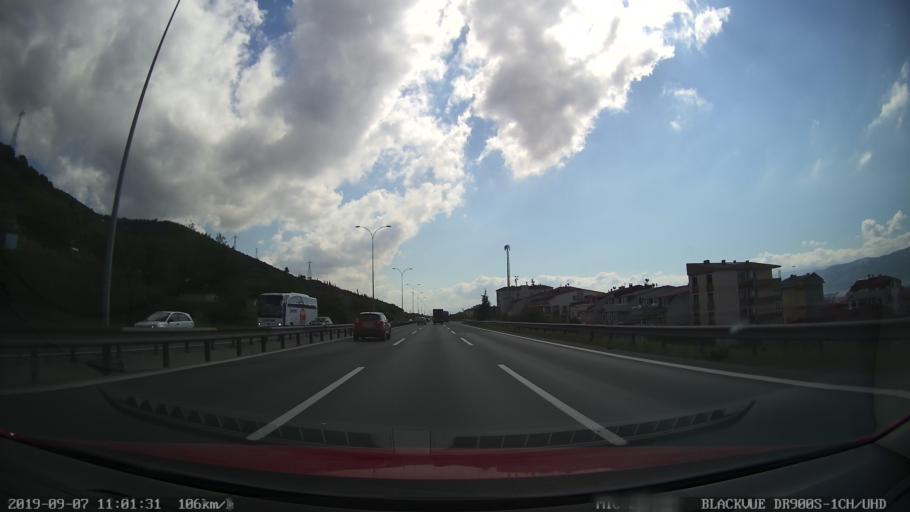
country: TR
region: Kocaeli
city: Korfez
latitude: 40.7784
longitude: 29.7474
